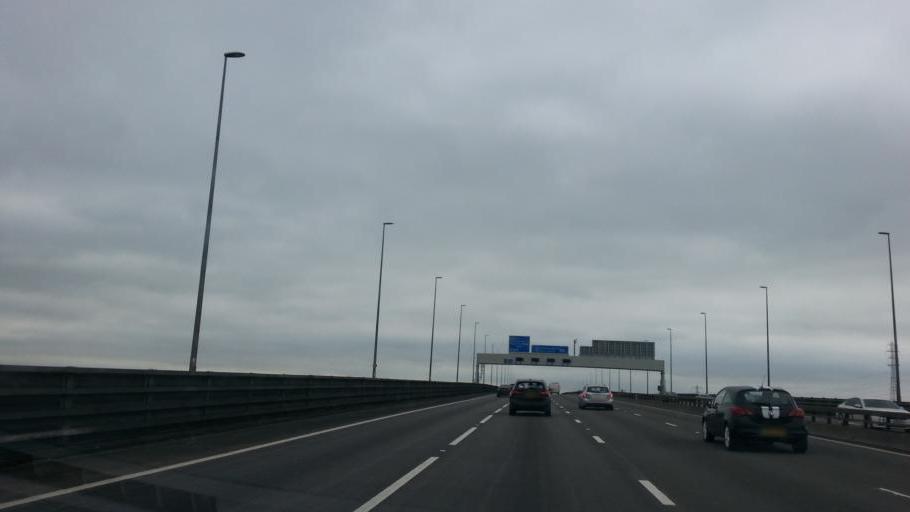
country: GB
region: England
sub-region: North Somerset
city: Easton-in-Gordano
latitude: 51.4921
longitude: -2.6892
